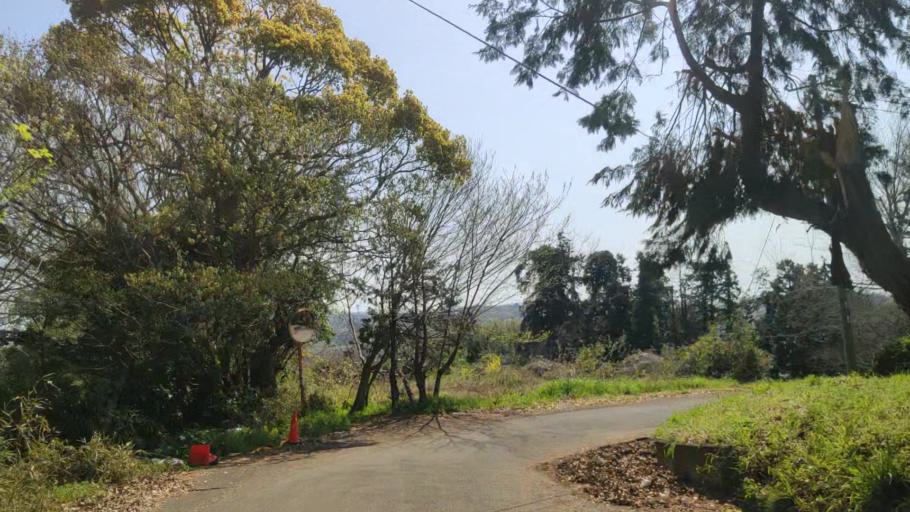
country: JP
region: Kanagawa
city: Ninomiya
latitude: 35.3208
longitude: 139.2734
